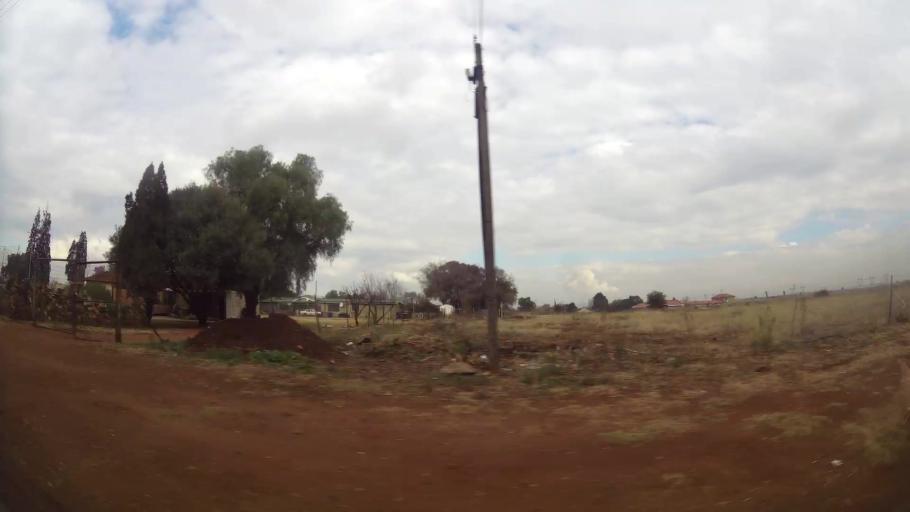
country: ZA
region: Gauteng
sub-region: Sedibeng District Municipality
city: Meyerton
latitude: -26.5931
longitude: 27.9944
